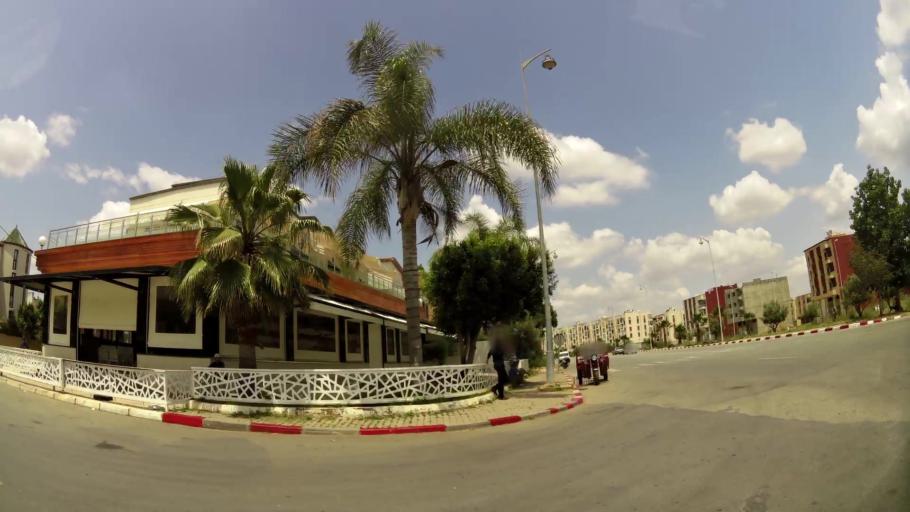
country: MA
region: Rabat-Sale-Zemmour-Zaer
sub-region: Khemisset
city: Tiflet
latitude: 34.0081
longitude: -6.5255
